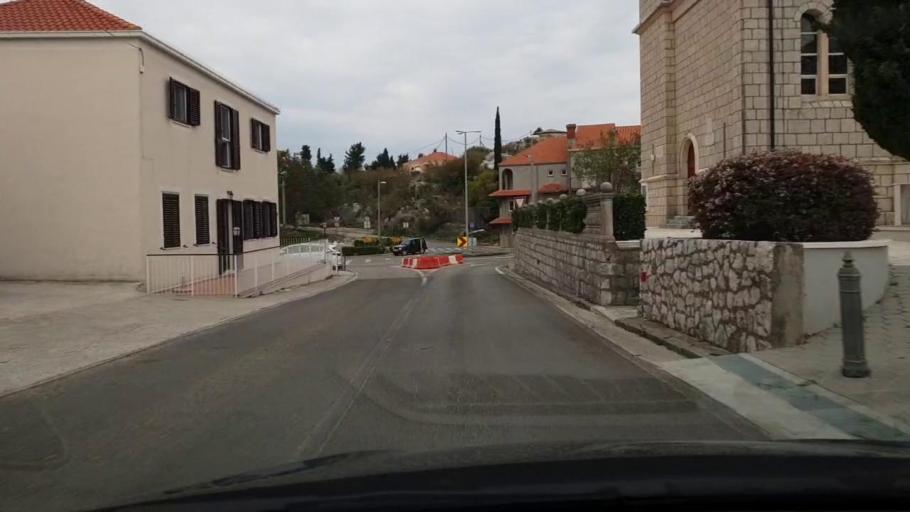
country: HR
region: Dubrovacko-Neretvanska
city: Cibaca
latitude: 42.6448
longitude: 18.1585
